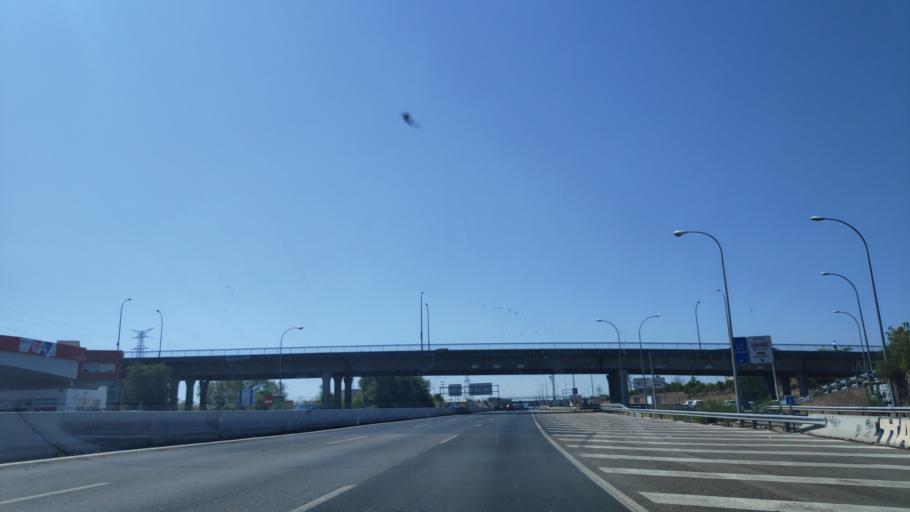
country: ES
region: Madrid
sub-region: Provincia de Madrid
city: Getafe
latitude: 40.3280
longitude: -3.7260
